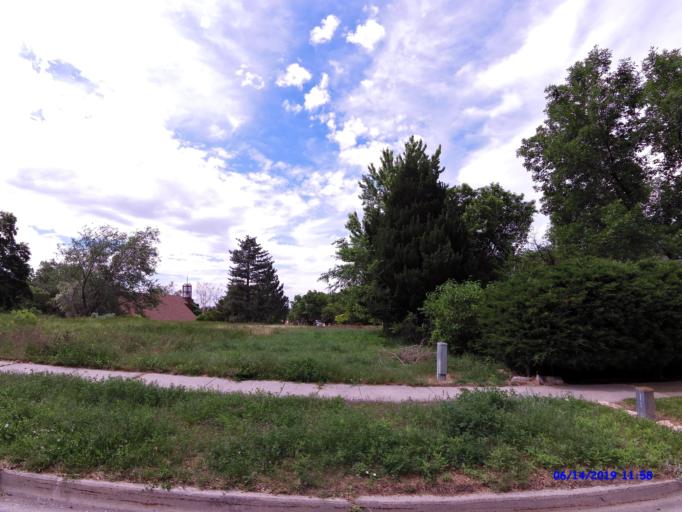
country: US
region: Utah
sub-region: Weber County
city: Harrisville
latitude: 41.2621
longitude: -111.9450
